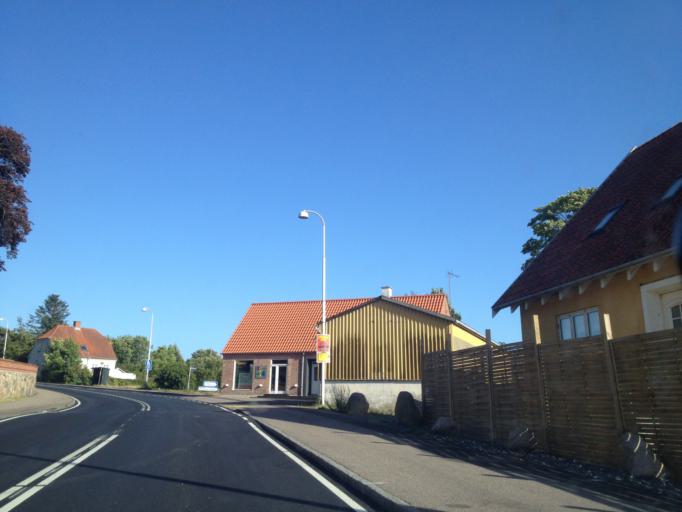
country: DK
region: Capital Region
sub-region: Gribskov Kommune
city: Helsinge
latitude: 56.0160
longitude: 12.1101
